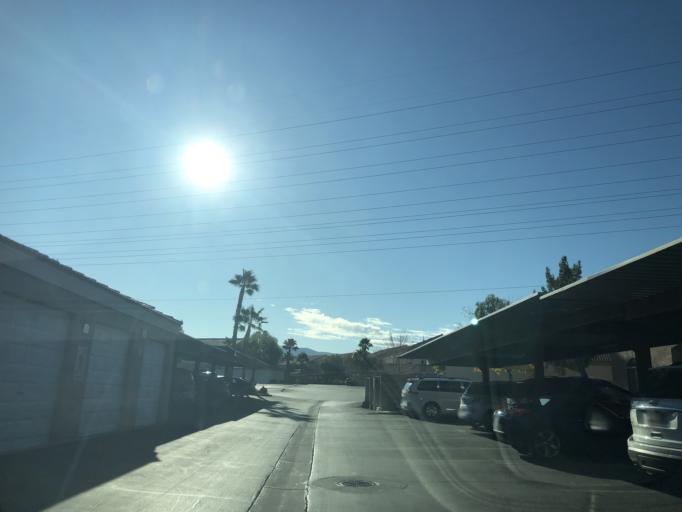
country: US
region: Nevada
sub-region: Clark County
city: Whitney
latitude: 36.0030
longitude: -115.0944
